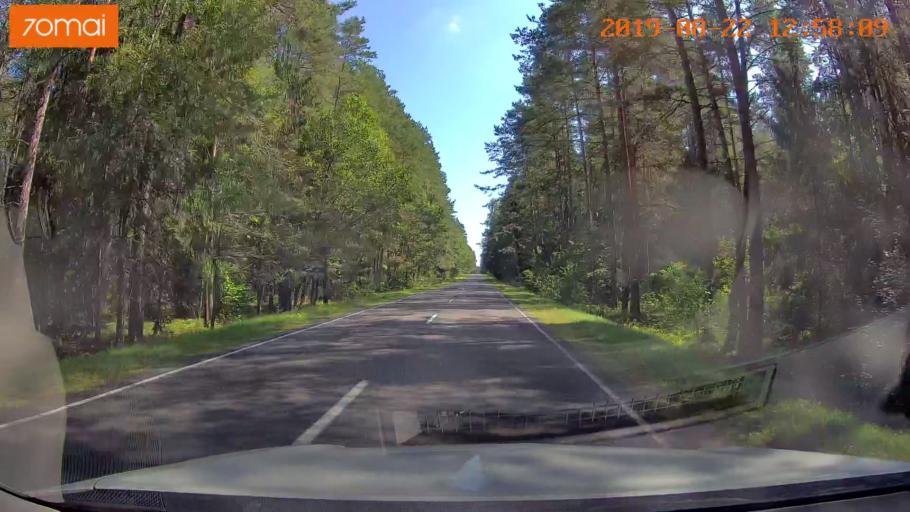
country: BY
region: Minsk
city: Prawdzinski
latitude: 53.4255
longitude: 27.7641
